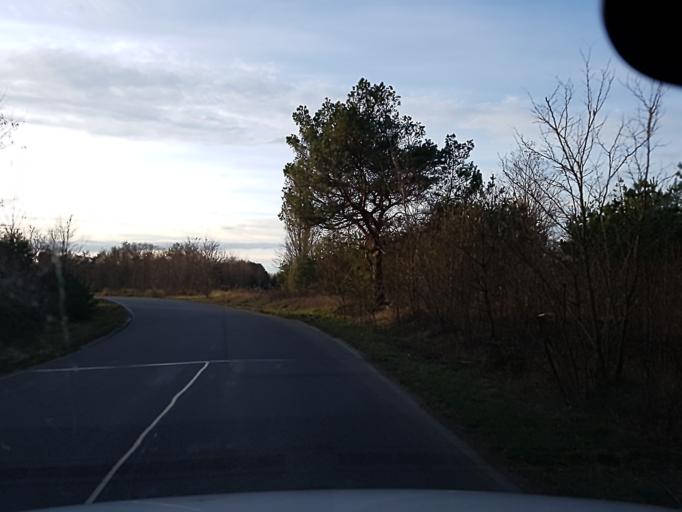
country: DE
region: Brandenburg
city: Finsterwalde
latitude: 51.6041
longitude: 13.7505
